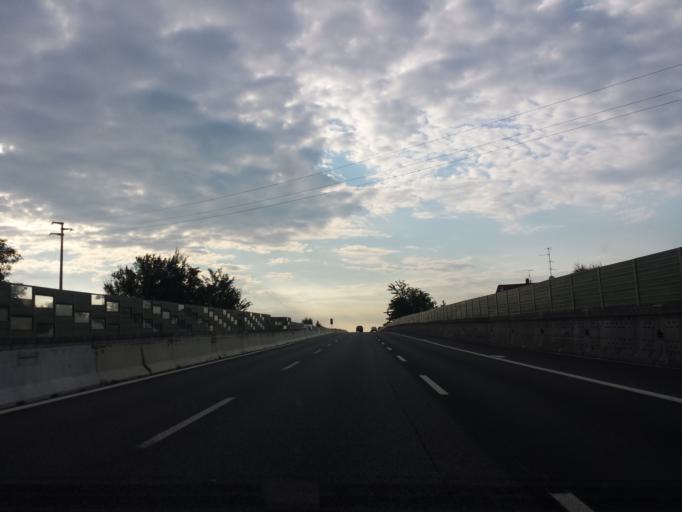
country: IT
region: Lombardy
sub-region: Provincia di Varese
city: Marnate
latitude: 45.6200
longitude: 8.9047
